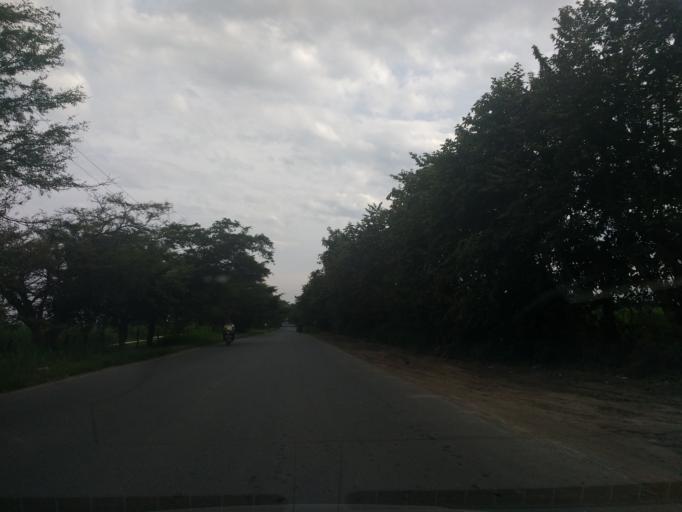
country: CO
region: Valle del Cauca
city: Florida
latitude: 3.2946
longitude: -76.2289
